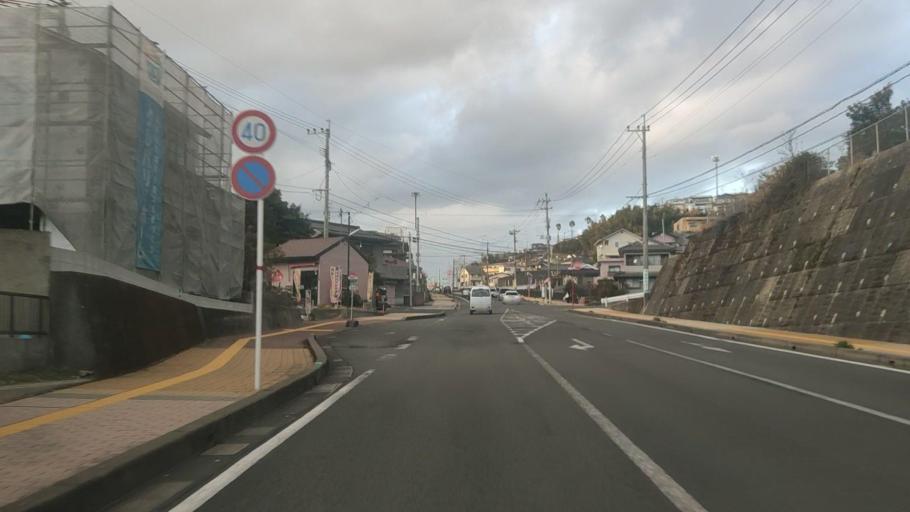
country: JP
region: Kagoshima
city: Kagoshima-shi
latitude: 31.6157
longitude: 130.5551
